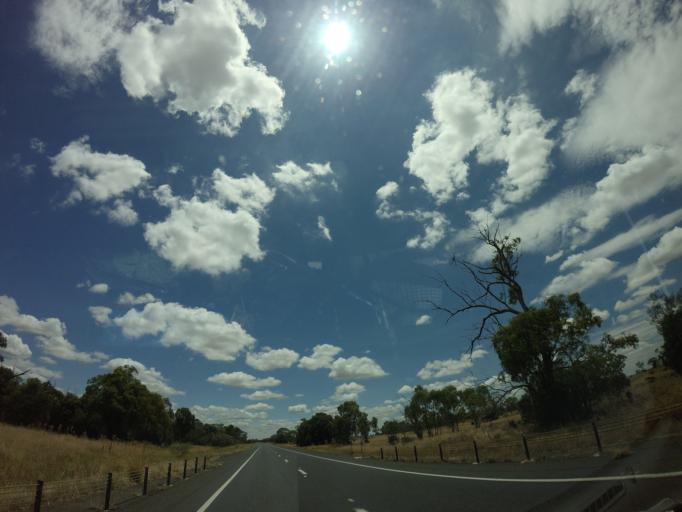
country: AU
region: New South Wales
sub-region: Moree Plains
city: Boggabilla
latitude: -28.8547
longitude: 150.2171
